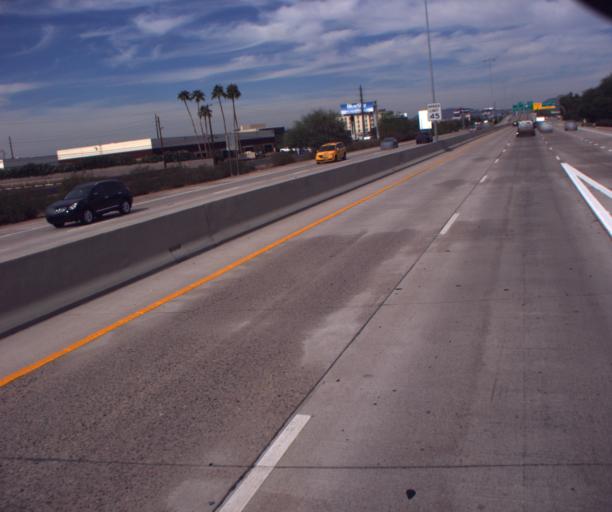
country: US
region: Arizona
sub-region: Maricopa County
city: Tempe Junction
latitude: 33.4146
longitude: -111.9782
